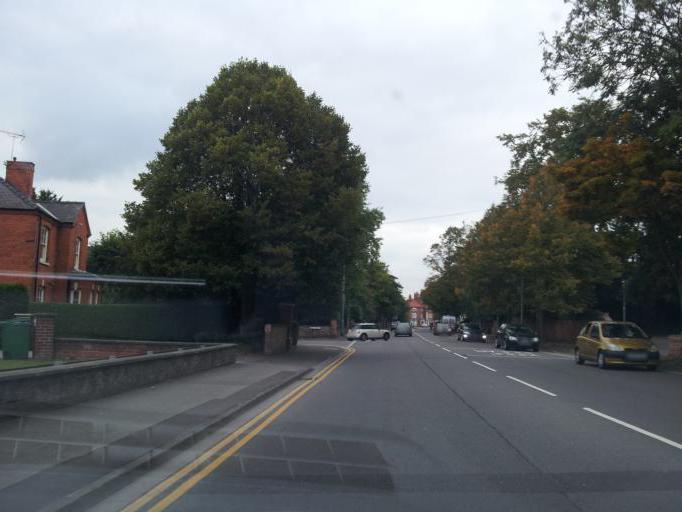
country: GB
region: England
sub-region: Nottinghamshire
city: Newark on Trent
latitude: 53.0723
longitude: -0.8061
